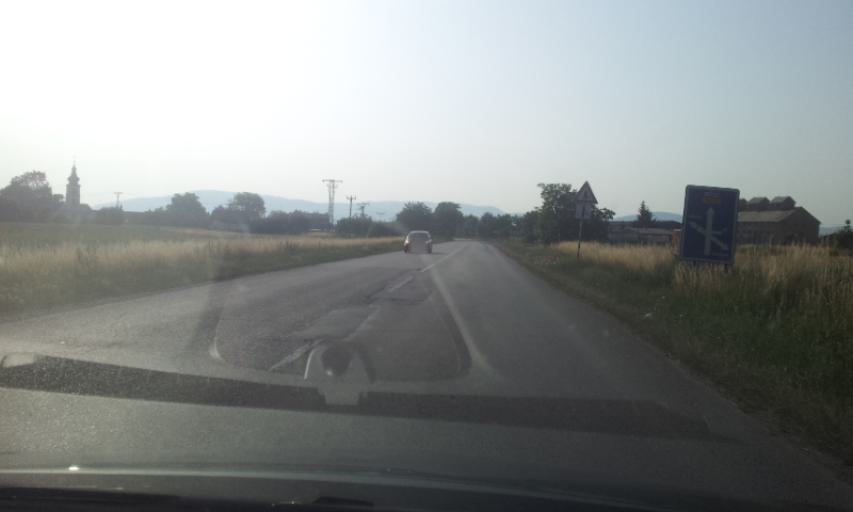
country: SK
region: Kosicky
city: Kosice
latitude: 48.6154
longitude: 21.2483
